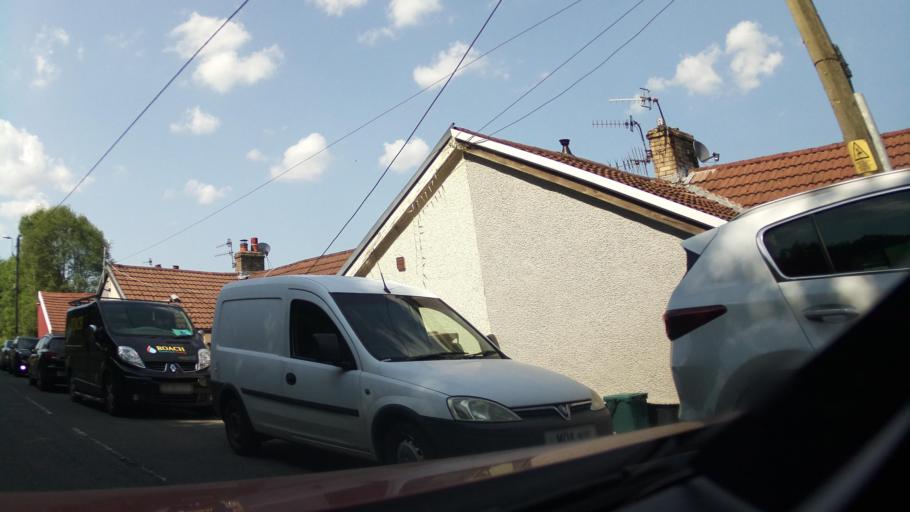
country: GB
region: Wales
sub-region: Caerphilly County Borough
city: New Tredegar
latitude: 51.7190
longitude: -3.2459
